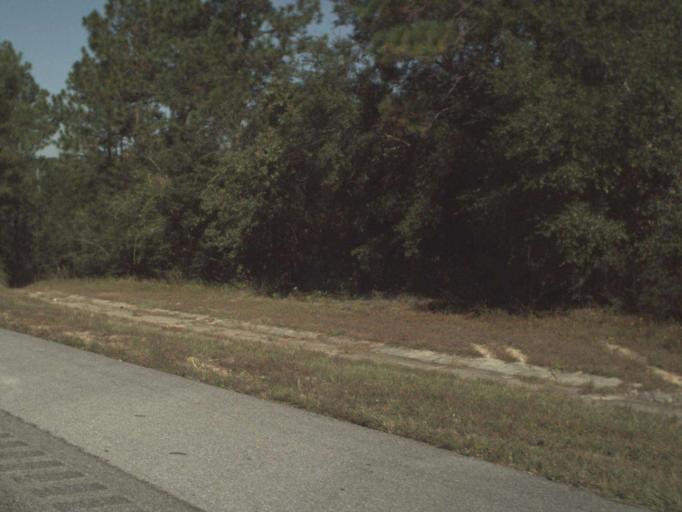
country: US
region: Florida
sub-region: Okaloosa County
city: Crestview
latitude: 30.7233
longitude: -86.4815
